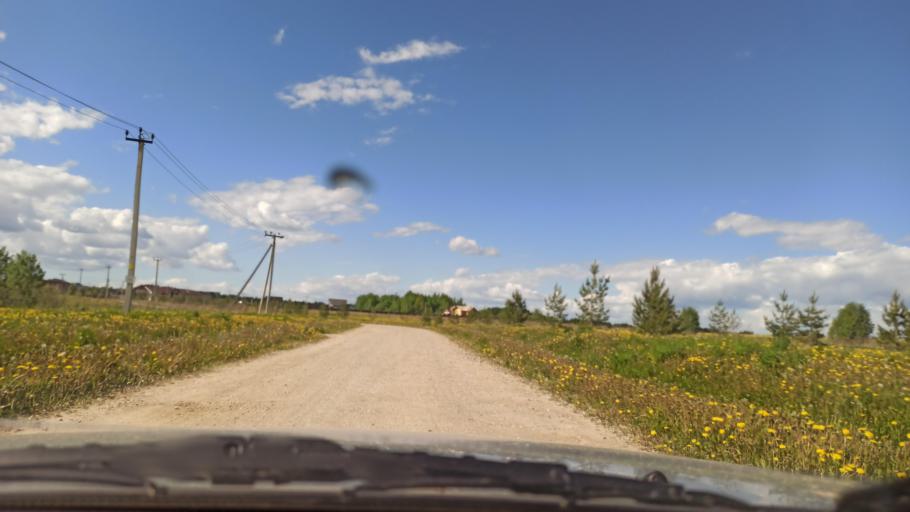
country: RU
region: Vologda
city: Molochnoye
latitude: 59.3721
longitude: 39.6955
